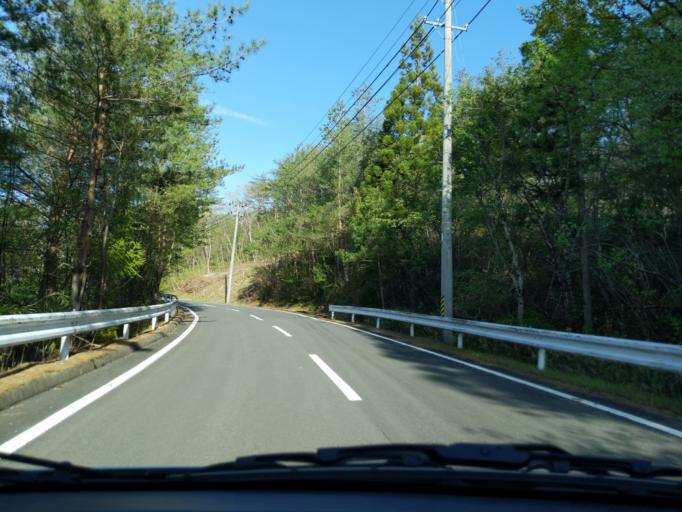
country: JP
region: Iwate
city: Ichinoseki
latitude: 38.8746
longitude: 140.9051
